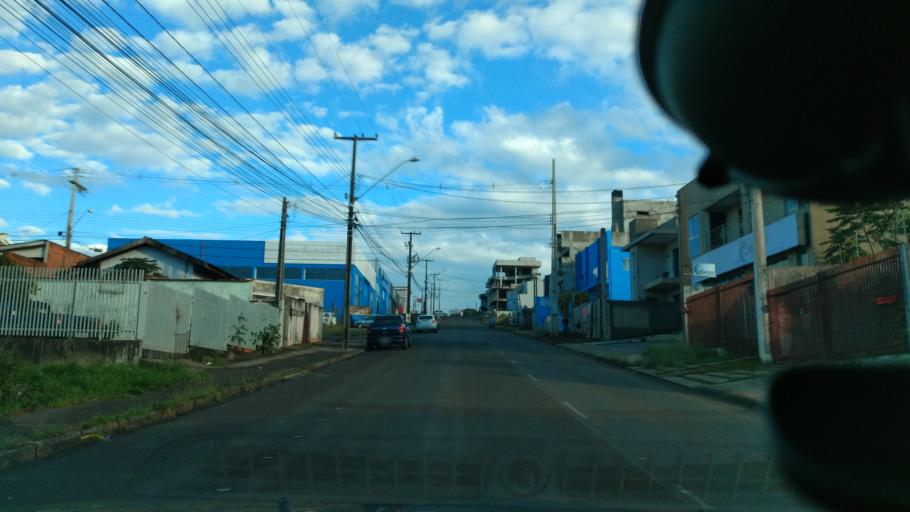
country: BR
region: Parana
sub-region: Guarapuava
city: Guarapuava
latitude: -25.3801
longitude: -51.4756
